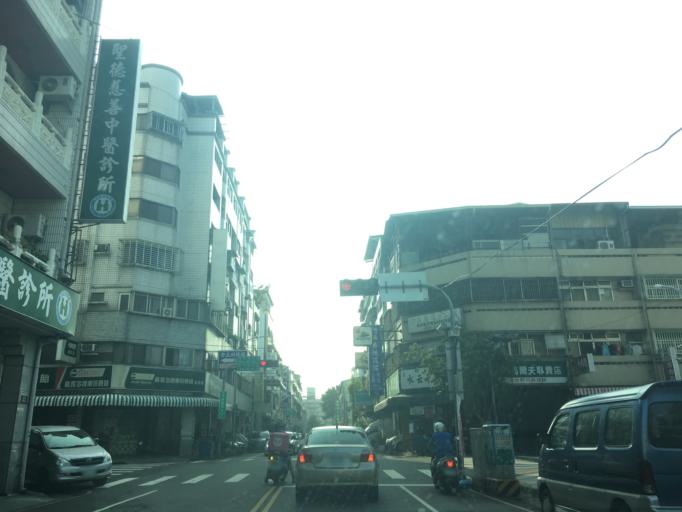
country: TW
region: Taiwan
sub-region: Taichung City
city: Taichung
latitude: 24.1682
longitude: 120.6867
